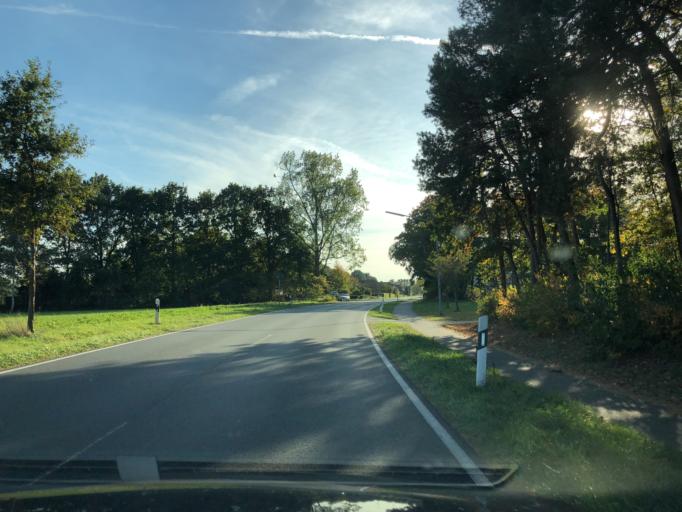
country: DE
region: Lower Saxony
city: Papenburg
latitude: 53.0451
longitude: 7.4034
